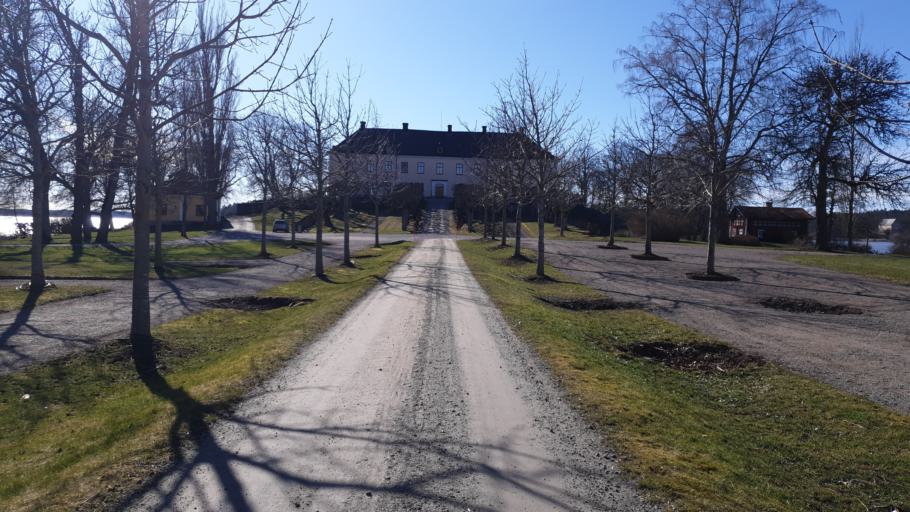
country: SE
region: Soedermanland
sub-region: Strangnas Kommun
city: Stallarholmen
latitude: 59.4732
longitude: 17.2481
